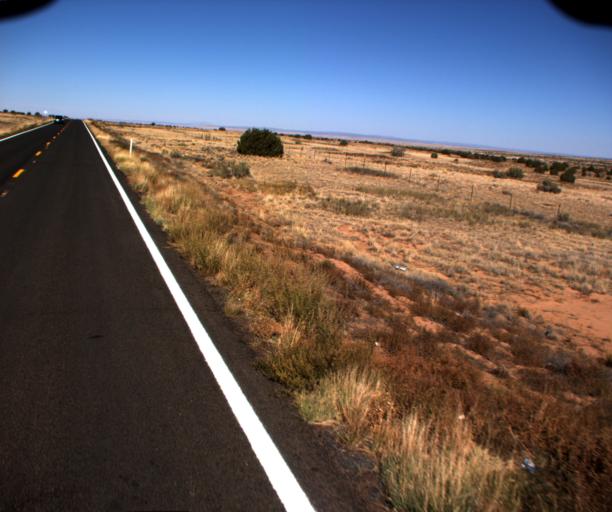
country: US
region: Arizona
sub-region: Coconino County
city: Tuba City
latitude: 35.9120
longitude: -110.8848
